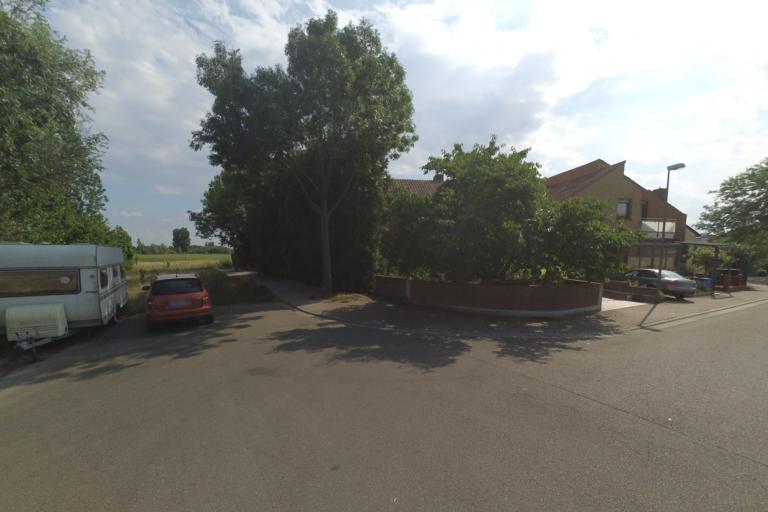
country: DE
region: Rheinland-Pfalz
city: Frankenthal
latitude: 49.5234
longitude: 8.3894
